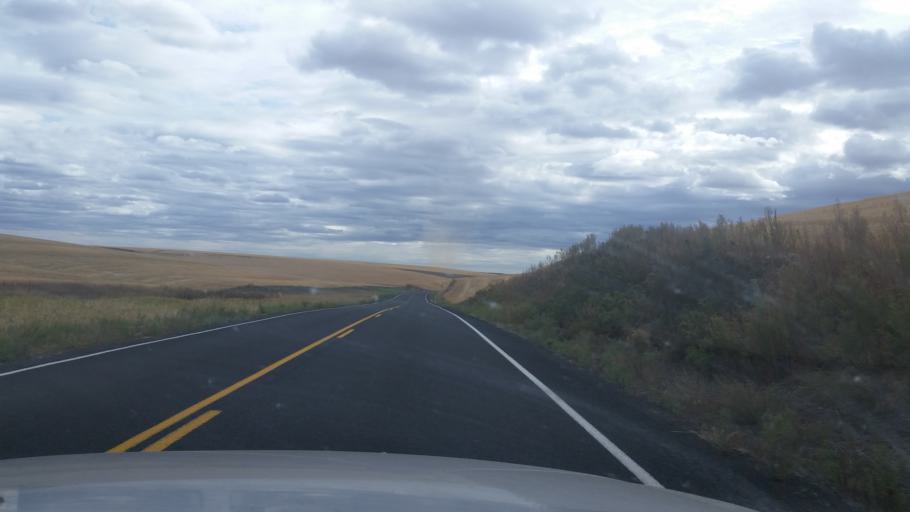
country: US
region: Washington
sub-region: Lincoln County
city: Davenport
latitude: 47.4758
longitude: -117.9510
